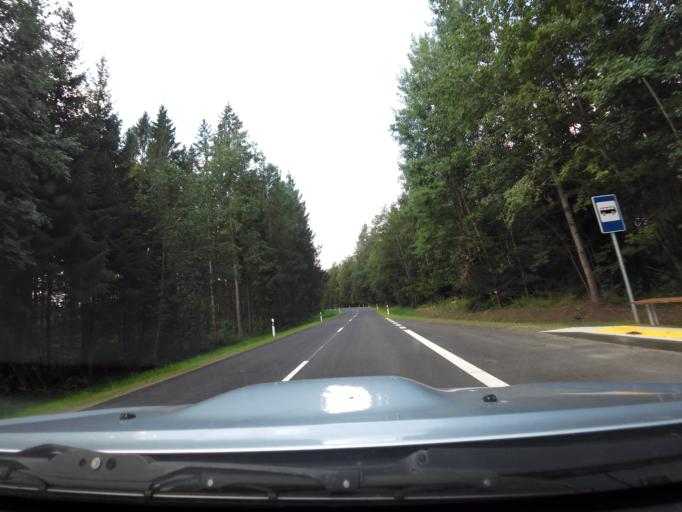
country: LT
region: Vilnius County
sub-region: Vilniaus Rajonas
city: Vievis
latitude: 54.8766
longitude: 24.8065
